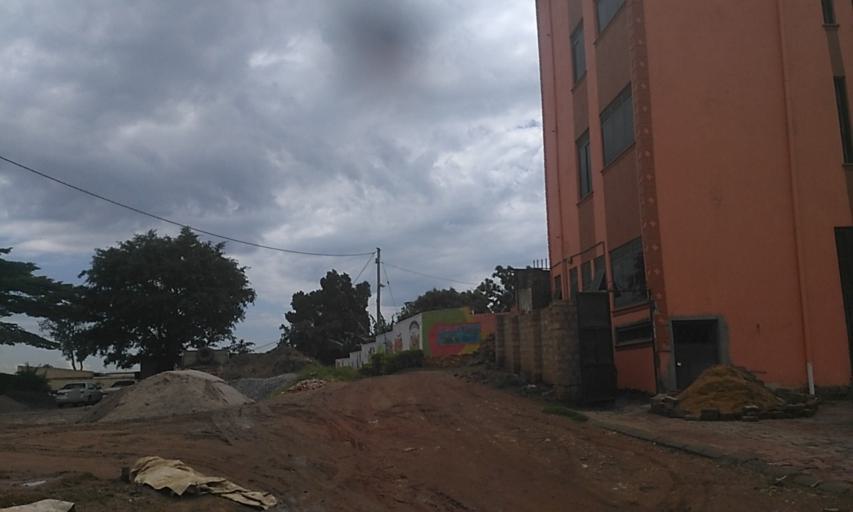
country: UG
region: Central Region
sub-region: Wakiso District
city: Kireka
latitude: 0.3678
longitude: 32.6486
